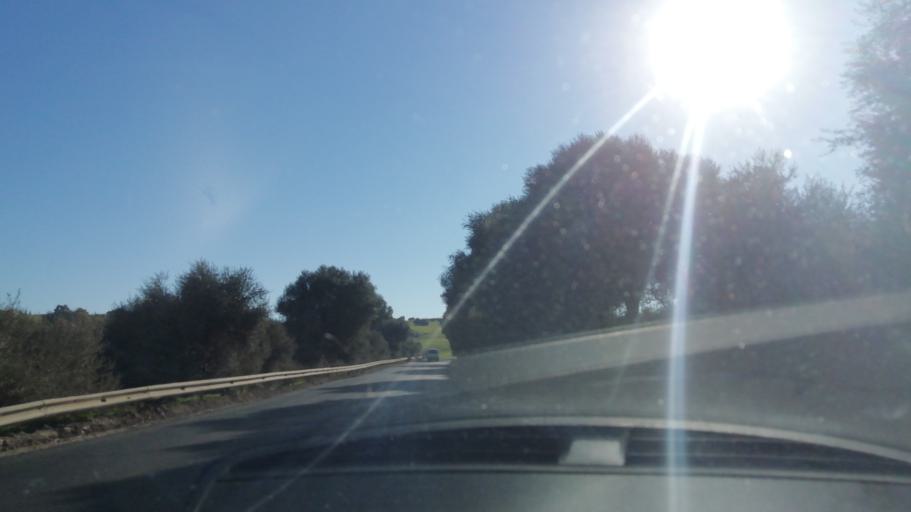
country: DZ
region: Relizane
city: Smala
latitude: 35.6641
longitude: 0.8120
